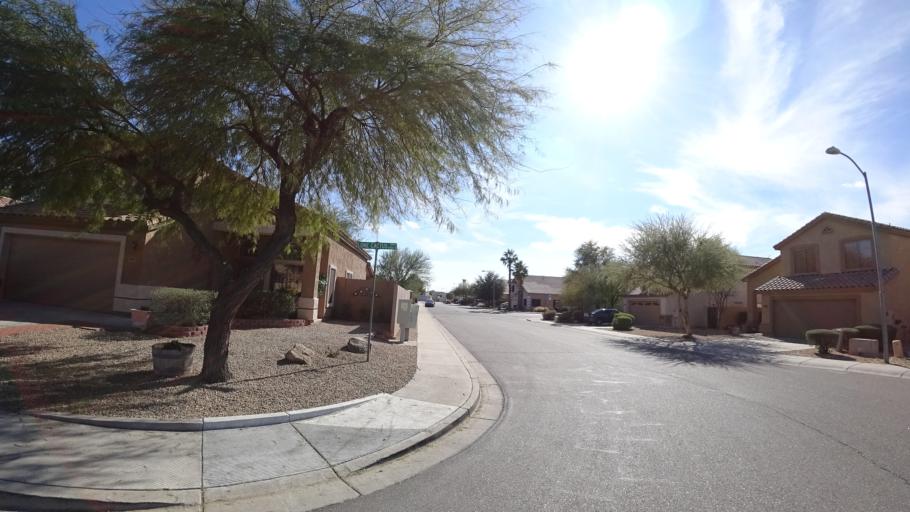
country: US
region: Arizona
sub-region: Maricopa County
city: Sun City
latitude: 33.6792
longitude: -112.2195
